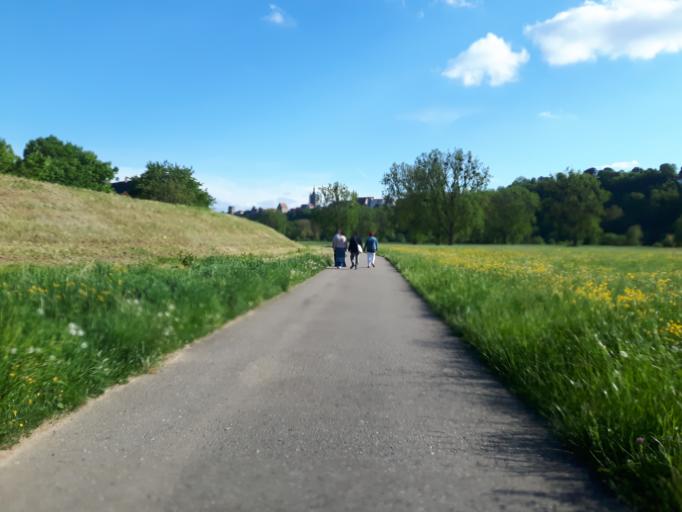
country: DE
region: Baden-Wuerttemberg
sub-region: Regierungsbezirk Stuttgart
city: Offenau
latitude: 49.2401
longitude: 9.1599
